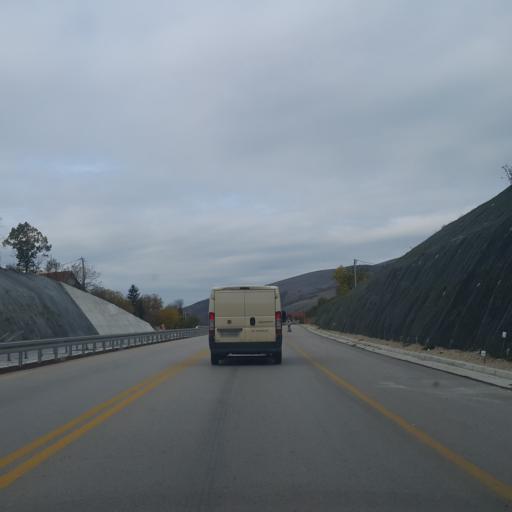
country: RS
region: Central Serbia
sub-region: Pirotski Okrug
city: Bela Palanka
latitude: 43.2202
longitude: 22.4096
